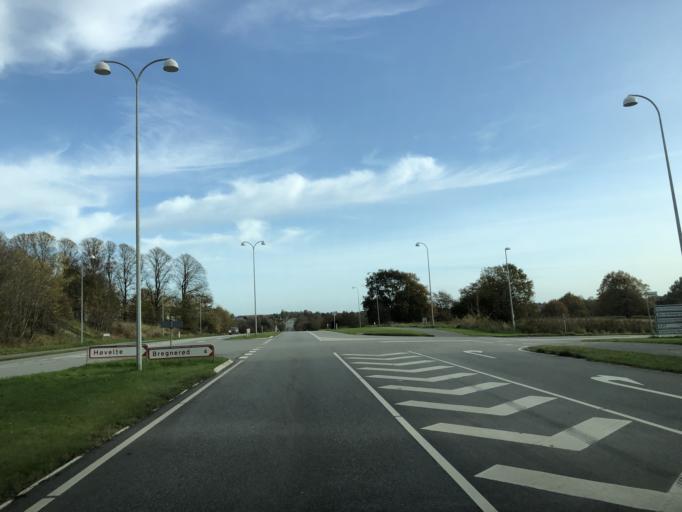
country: DK
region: Capital Region
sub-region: Allerod Kommune
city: Blovstrod
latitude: 55.8578
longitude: 12.4030
